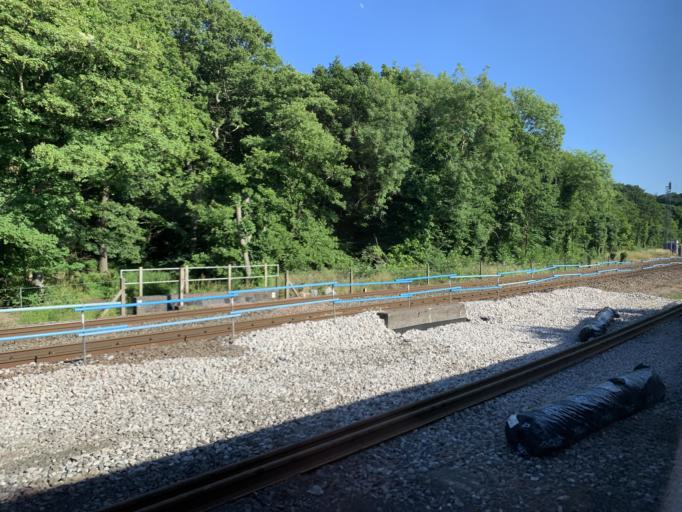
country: GB
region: England
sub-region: Derbyshire
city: Dronfield
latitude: 53.3295
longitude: -1.5149
